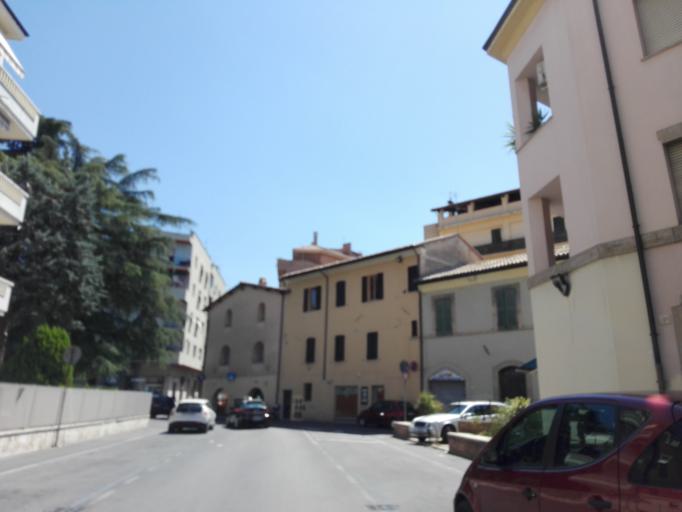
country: IT
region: Umbria
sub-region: Provincia di Perugia
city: Foligno
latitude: 42.9582
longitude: 12.7029
